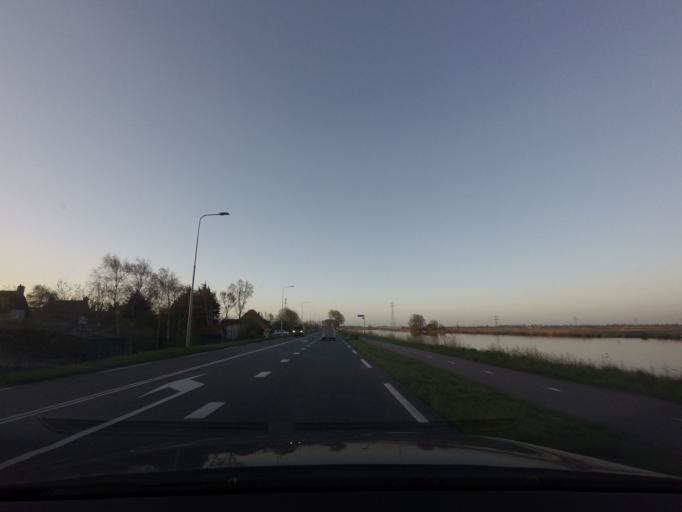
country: NL
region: North Holland
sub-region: Gemeente Uitgeest
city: Uitgeest
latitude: 52.5312
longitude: 4.7782
